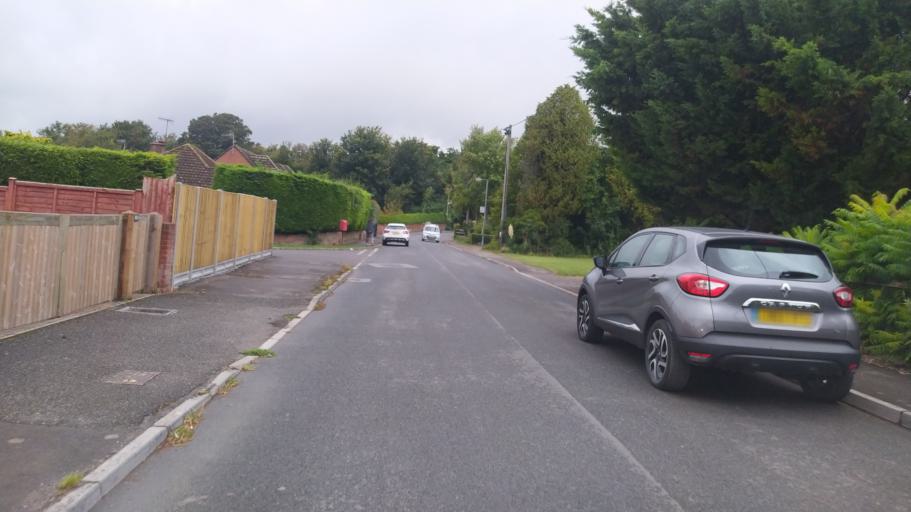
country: GB
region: England
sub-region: Wiltshire
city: Allington
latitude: 51.1194
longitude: -1.7314
